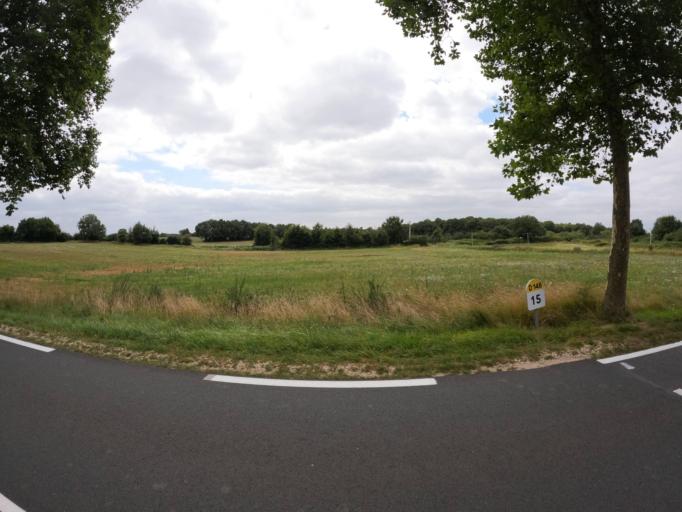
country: FR
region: Poitou-Charentes
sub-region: Departement de la Vienne
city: Charroux
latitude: 46.1387
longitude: 0.4360
